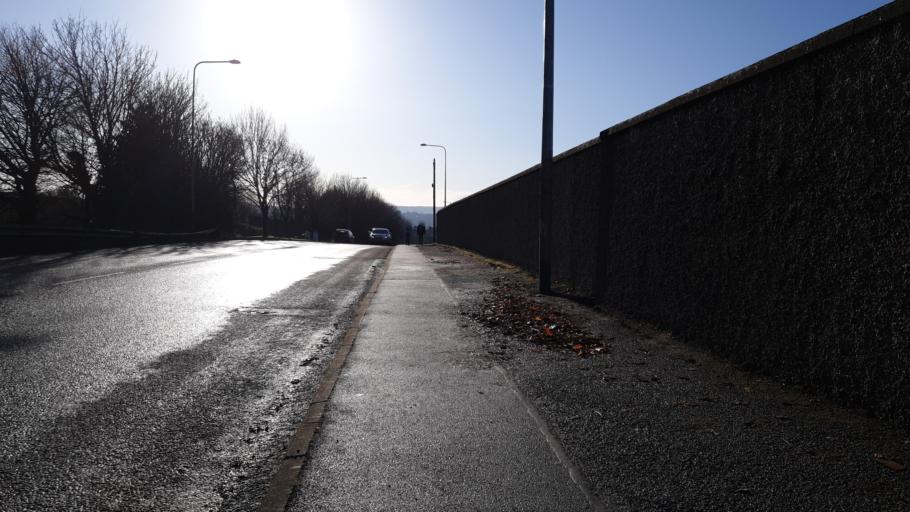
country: IE
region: Munster
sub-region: County Cork
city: Cork
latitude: 51.8906
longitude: -8.4334
